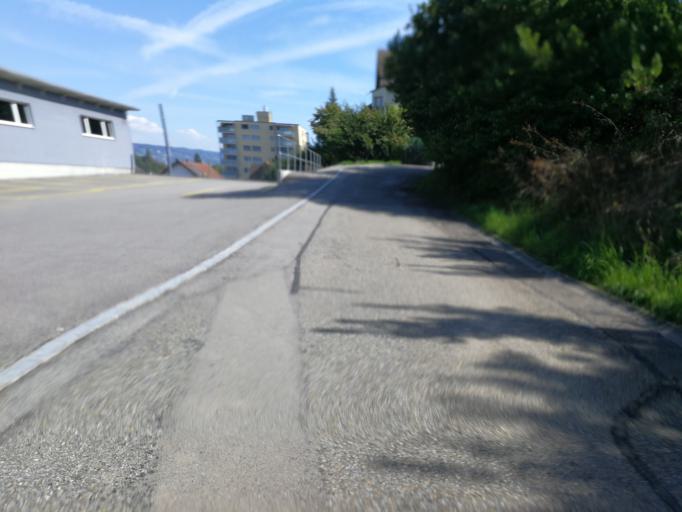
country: CH
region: Zurich
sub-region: Bezirk Horgen
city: Au
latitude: 47.2461
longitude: 8.6420
